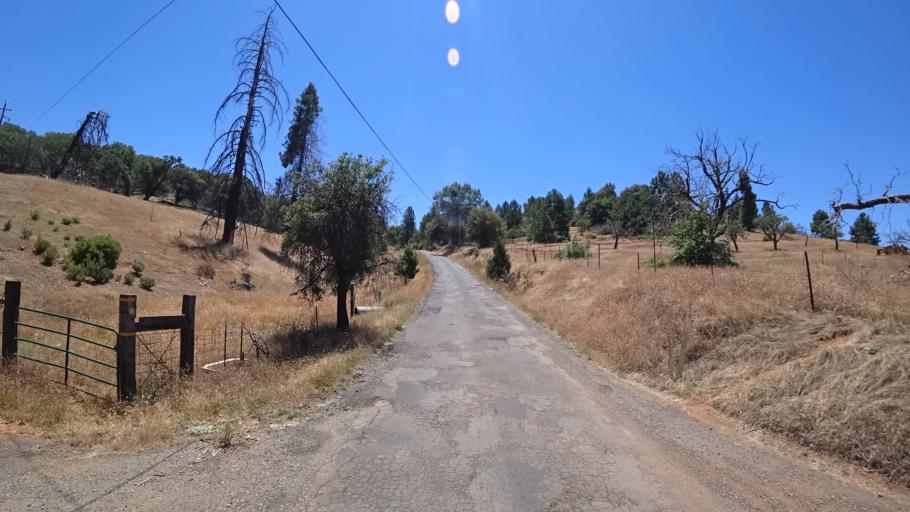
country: US
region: California
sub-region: Calaveras County
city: Mountain Ranch
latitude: 38.2328
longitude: -120.6029
